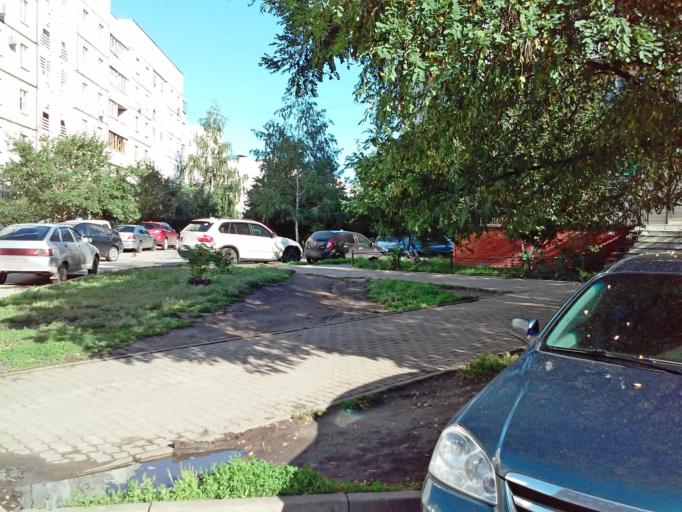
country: RU
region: Belgorod
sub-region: Belgorodskiy Rayon
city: Belgorod
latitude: 50.5557
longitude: 36.5710
